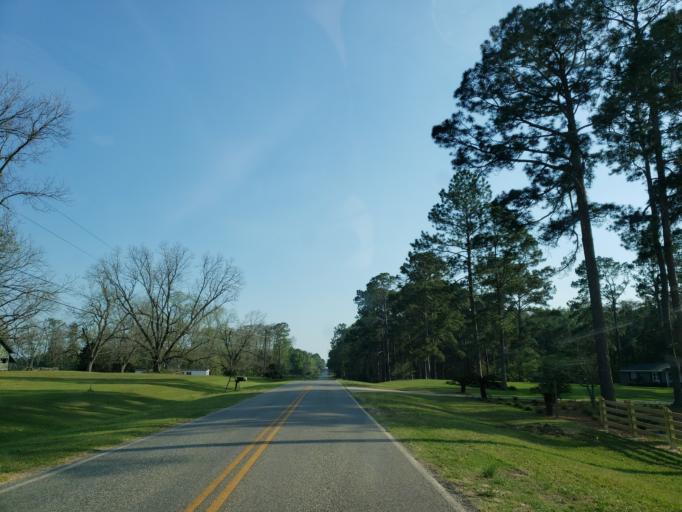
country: US
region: Georgia
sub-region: Tift County
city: Tifton
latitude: 31.5281
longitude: -83.5598
